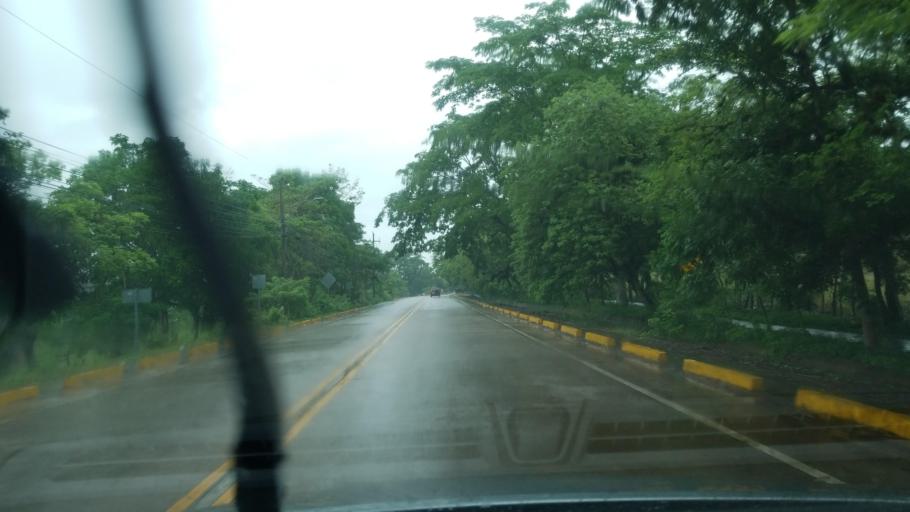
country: HN
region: Copan
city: Copan
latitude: 14.8392
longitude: -89.1486
